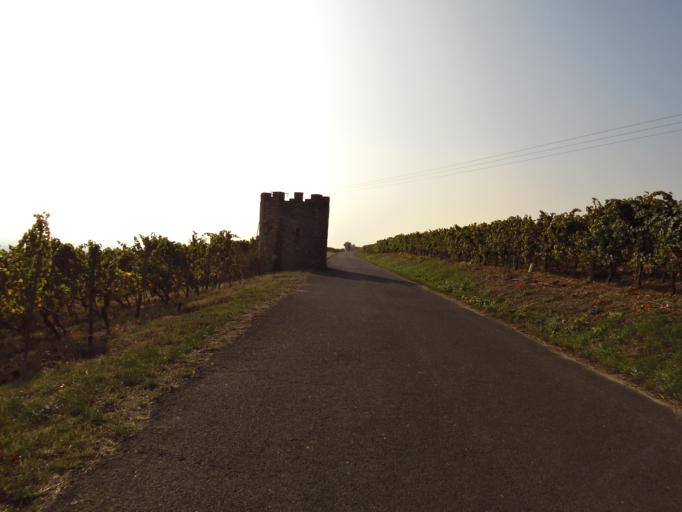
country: DE
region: Rheinland-Pfalz
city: Kindenheim
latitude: 49.6053
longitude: 8.1737
